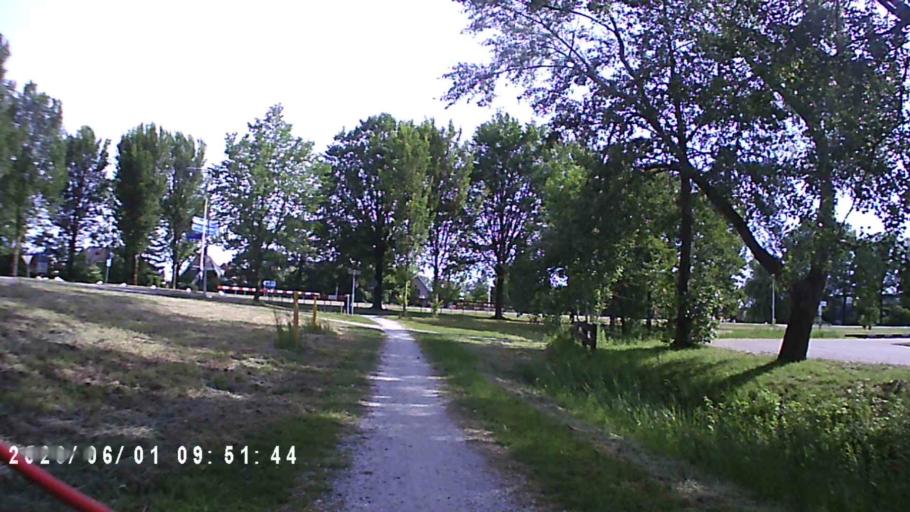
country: NL
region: Friesland
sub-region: Menameradiel
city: Berltsum
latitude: 53.2425
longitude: 5.6596
